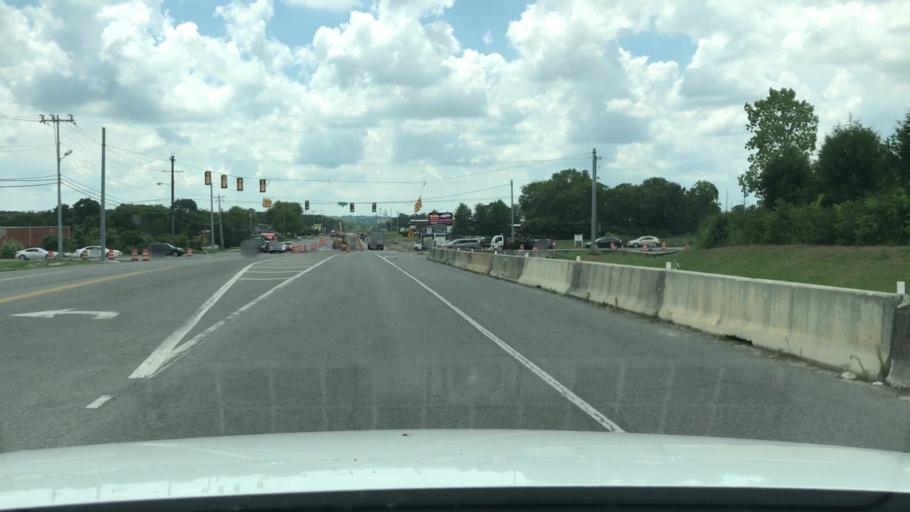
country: US
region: Tennessee
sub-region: Sumner County
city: Gallatin
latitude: 36.3645
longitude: -86.4402
